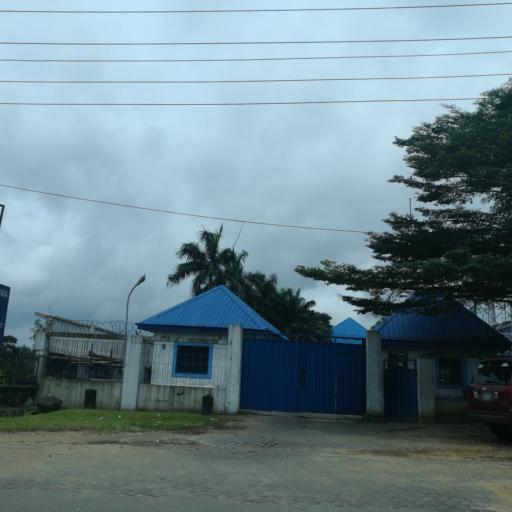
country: NG
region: Rivers
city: Port Harcourt
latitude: 4.7865
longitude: 7.0048
